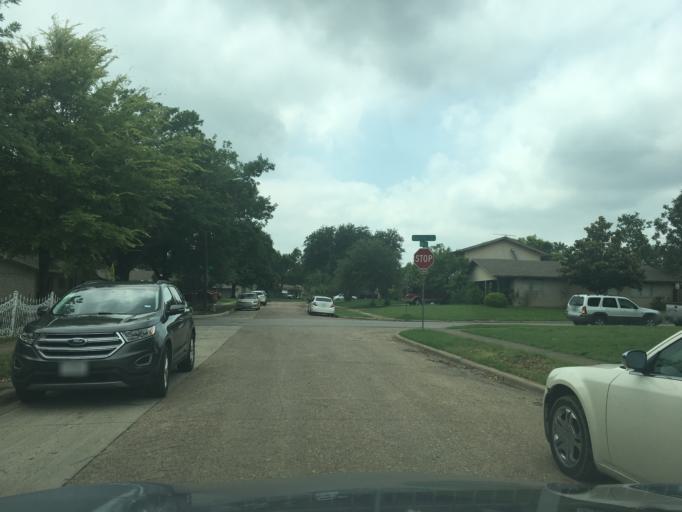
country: US
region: Texas
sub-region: Dallas County
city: Richardson
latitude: 32.9362
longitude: -96.7638
